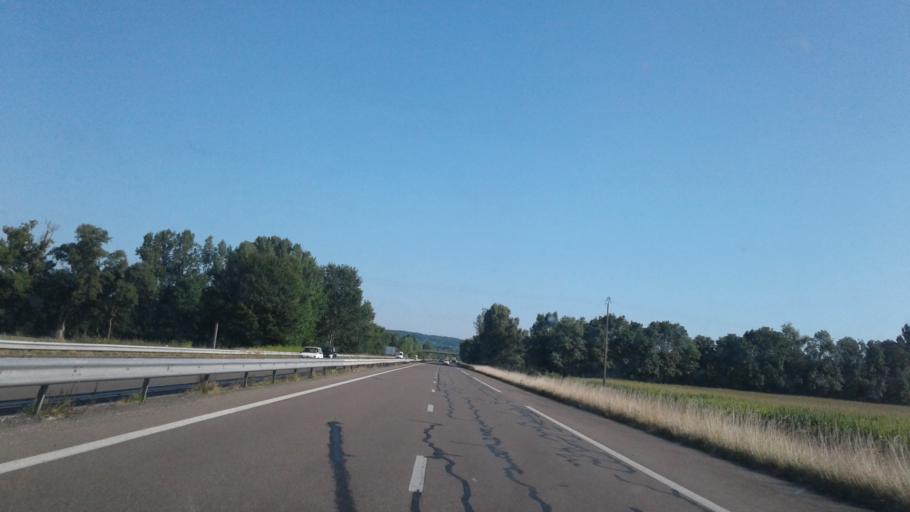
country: FR
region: Rhone-Alpes
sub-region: Departement de l'Ain
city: Priay
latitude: 46.0018
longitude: 5.3127
